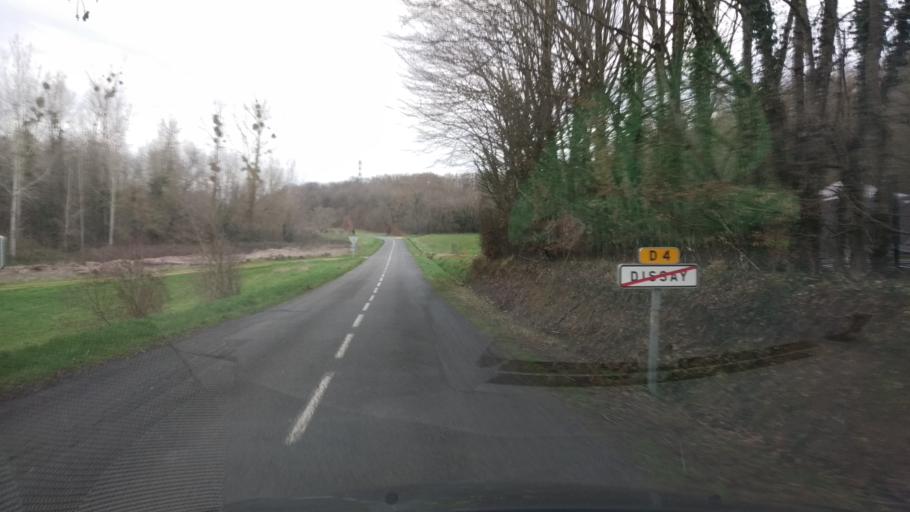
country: FR
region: Poitou-Charentes
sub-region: Departement de la Vienne
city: Dissay
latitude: 46.7040
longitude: 0.4329
